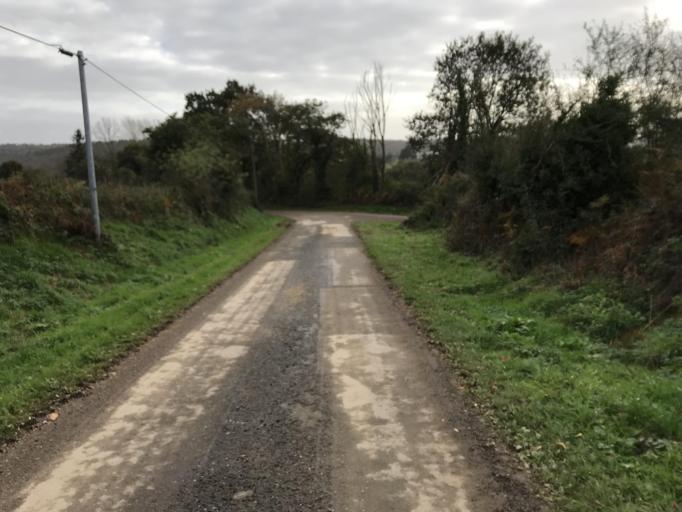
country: FR
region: Brittany
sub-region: Departement du Finistere
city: Irvillac
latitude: 48.3511
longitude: -4.2178
